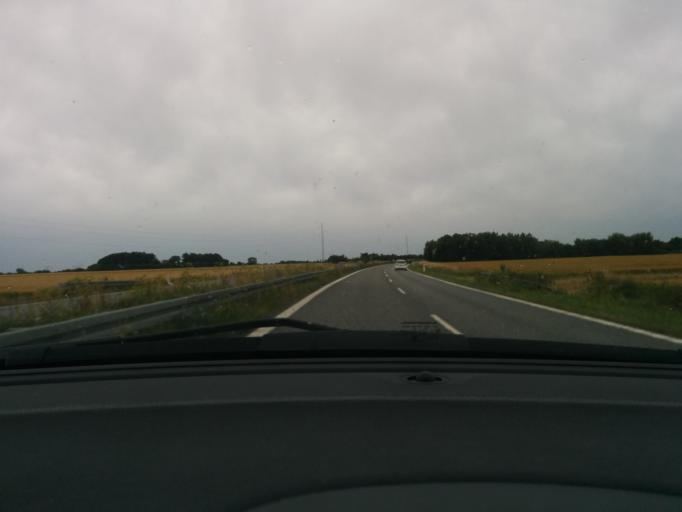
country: DK
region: Zealand
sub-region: Lolland Kommune
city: Rodby
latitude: 54.6820
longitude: 11.3993
